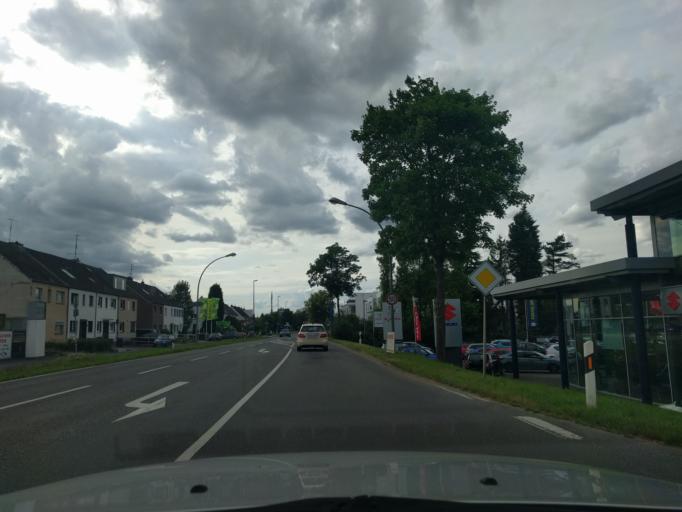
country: DE
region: North Rhine-Westphalia
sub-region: Regierungsbezirk Dusseldorf
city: Meerbusch
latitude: 51.2390
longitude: 6.7080
